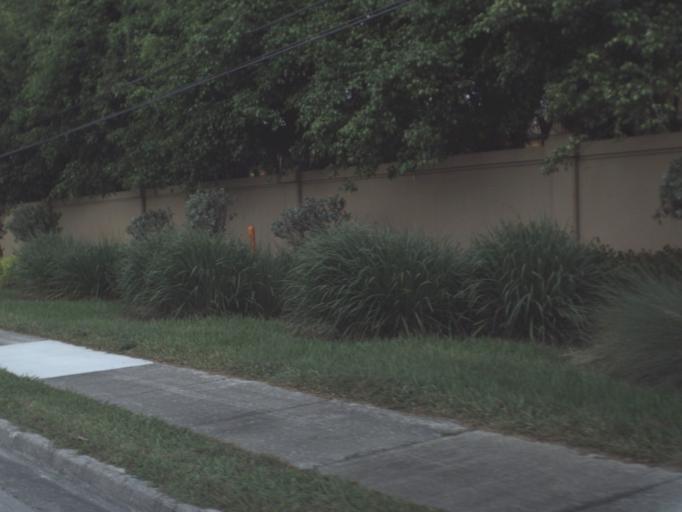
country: US
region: Florida
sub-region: Collier County
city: Lely Resort
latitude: 26.0774
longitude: -81.6885
